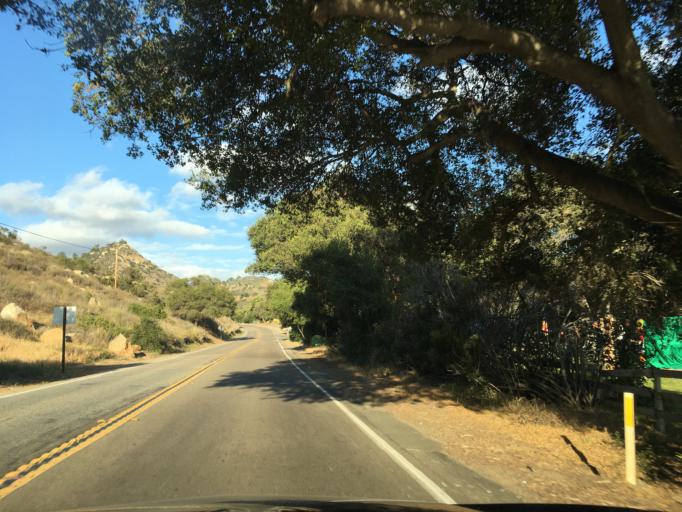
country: US
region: California
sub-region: San Diego County
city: Hidden Meadows
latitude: 33.2515
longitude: -117.1214
